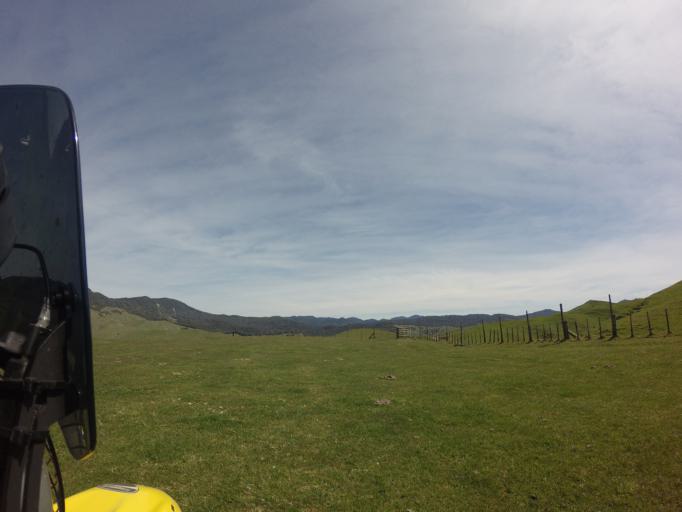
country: NZ
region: Bay of Plenty
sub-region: Opotiki District
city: Opotiki
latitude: -38.4726
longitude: 177.3770
